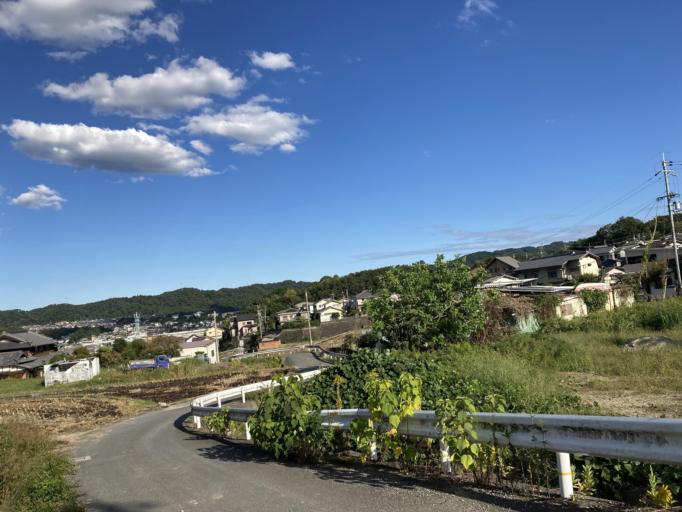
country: JP
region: Nara
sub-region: Ikoma-shi
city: Ikoma
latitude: 34.6694
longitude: 135.6984
